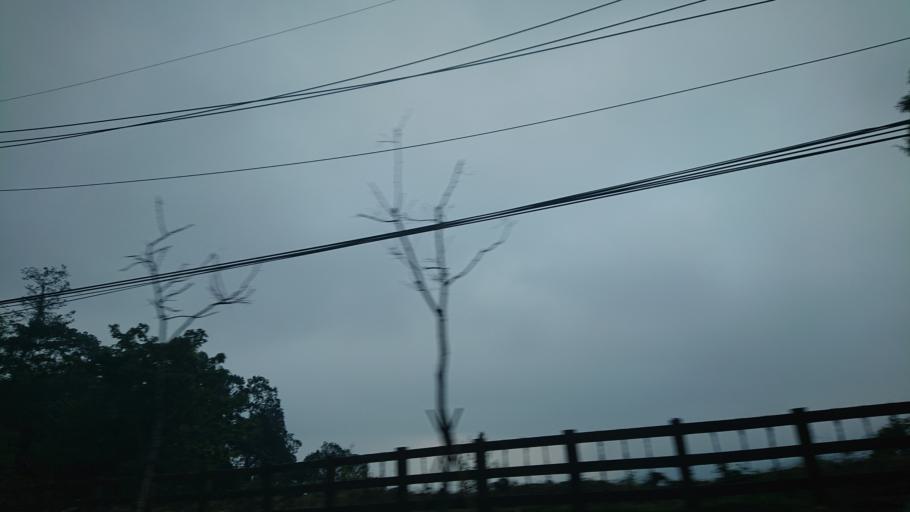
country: TW
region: Taiwan
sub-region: Chiayi
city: Jiayi Shi
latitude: 23.4699
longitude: 120.7186
